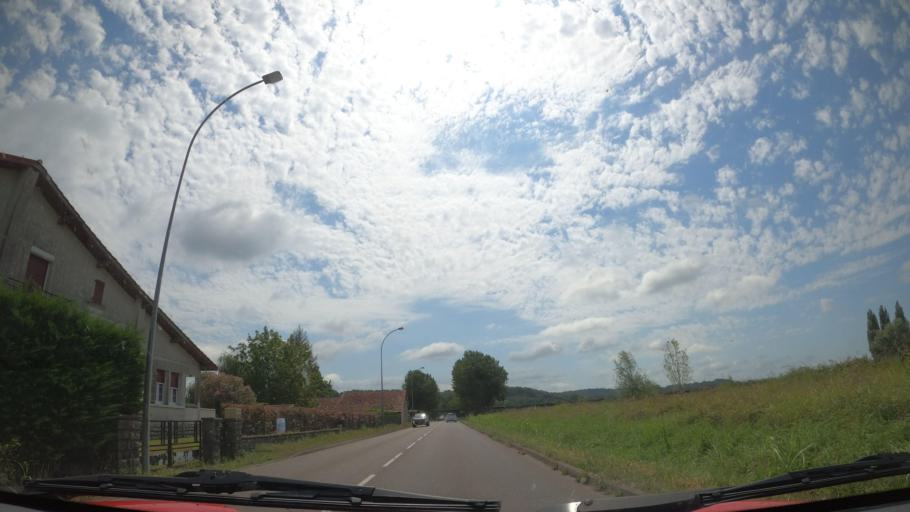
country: FR
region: Aquitaine
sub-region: Departement des Landes
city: Peyrehorade
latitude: 43.5372
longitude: -1.1082
